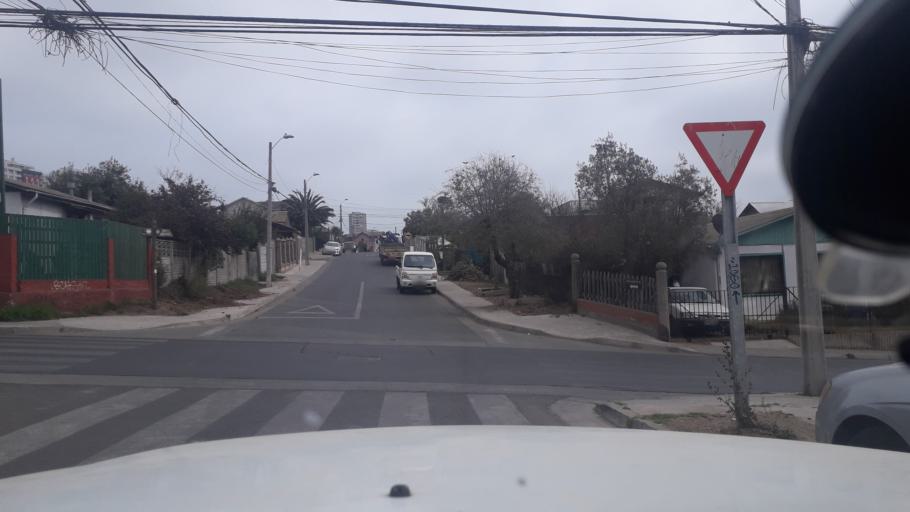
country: CL
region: Valparaiso
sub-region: Provincia de Valparaiso
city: Vina del Mar
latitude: -32.9359
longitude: -71.5263
